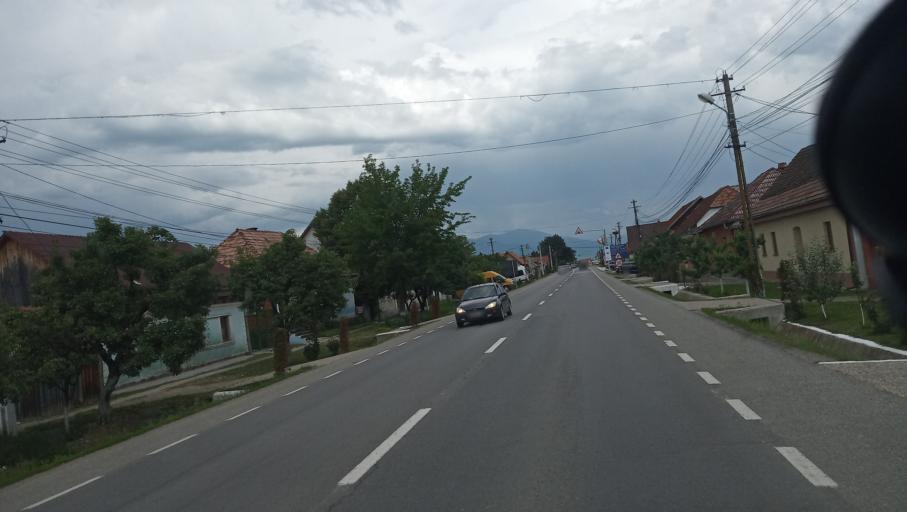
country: RO
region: Bistrita-Nasaud
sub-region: Comuna Livezile
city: Livezile
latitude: 47.1827
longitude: 24.5887
